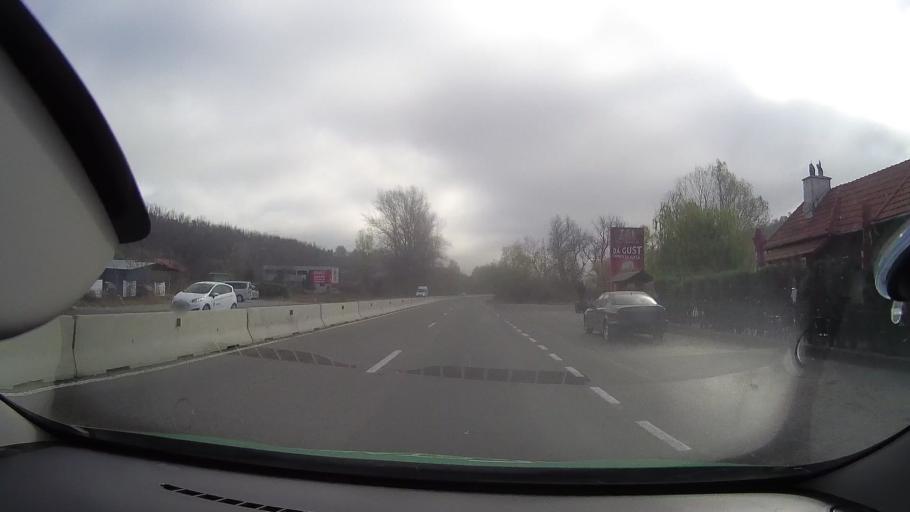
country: RO
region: Prahova
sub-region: Municipiul Campina
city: Campina
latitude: 45.1215
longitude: 25.7255
